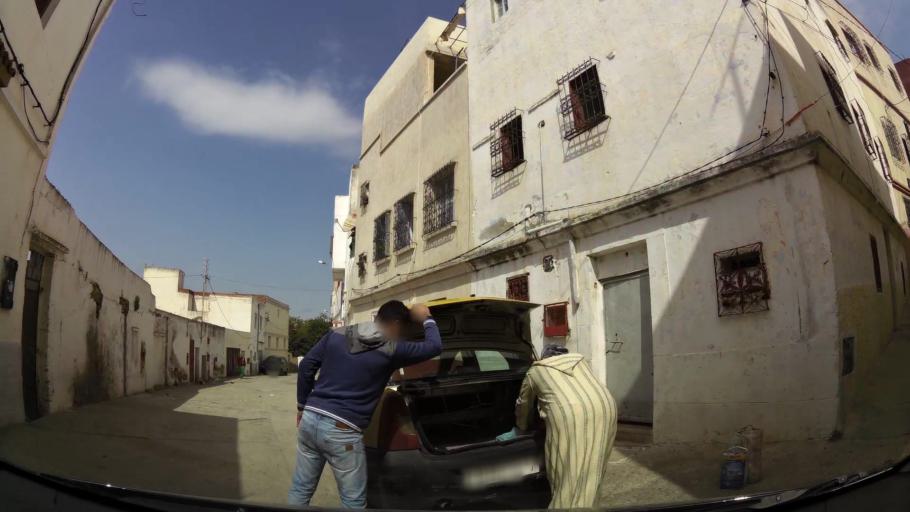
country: MA
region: Tanger-Tetouan
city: Tetouan
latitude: 35.5764
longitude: -5.3845
